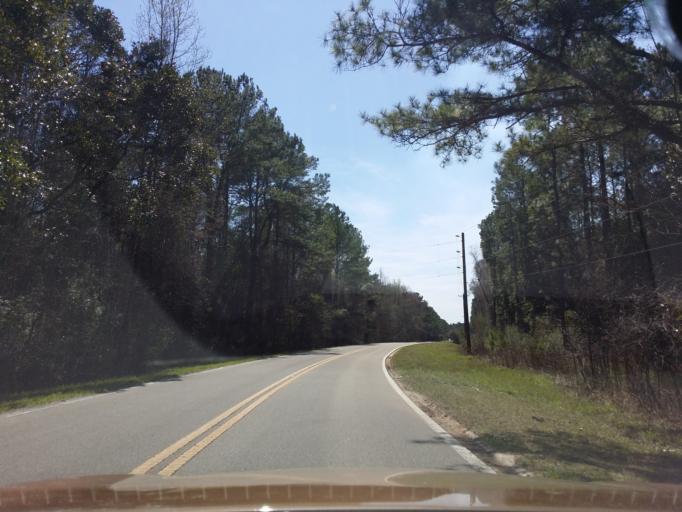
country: US
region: Florida
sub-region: Leon County
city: Woodville
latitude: 30.3273
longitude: -84.1467
